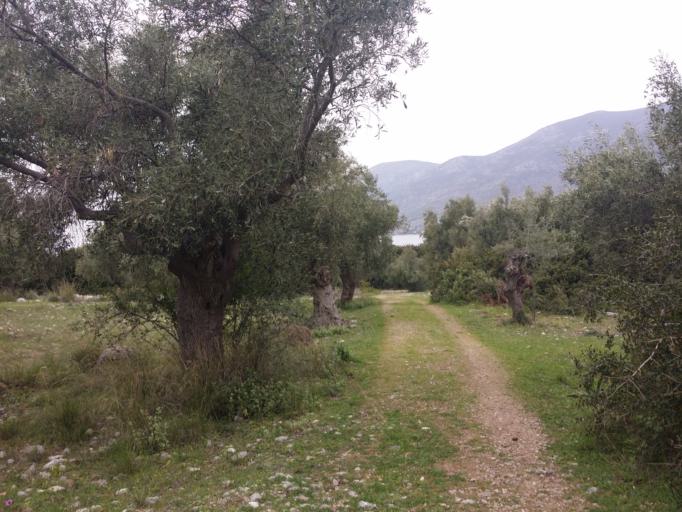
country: GR
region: Central Greece
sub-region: Nomos Voiotias
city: Kaparellion
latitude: 38.1480
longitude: 23.2258
